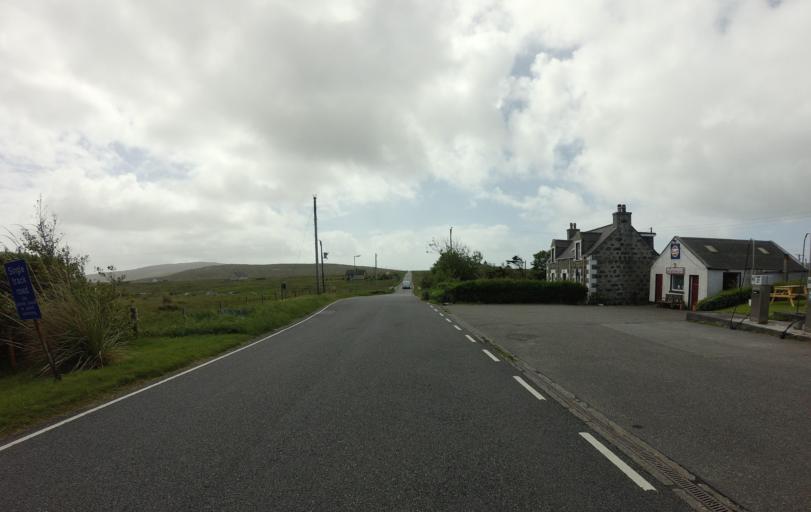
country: GB
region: Scotland
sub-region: Eilean Siar
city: Isle of South Uist
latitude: 57.1582
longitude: -7.3702
